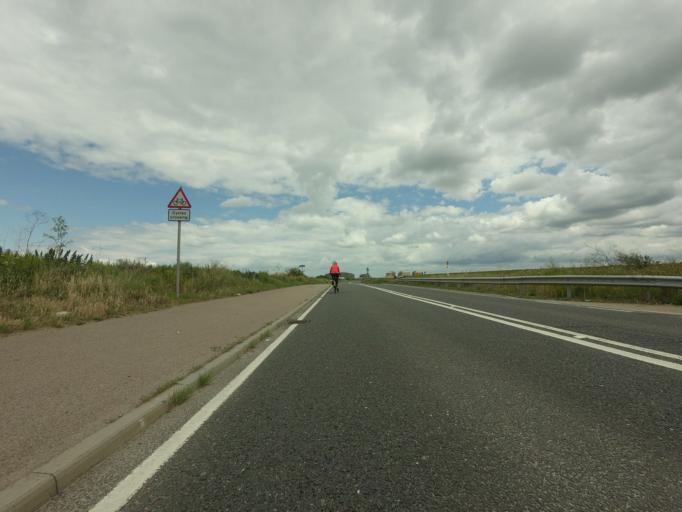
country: GB
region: England
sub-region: Medway
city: Allhallows
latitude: 51.4493
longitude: 0.6540
